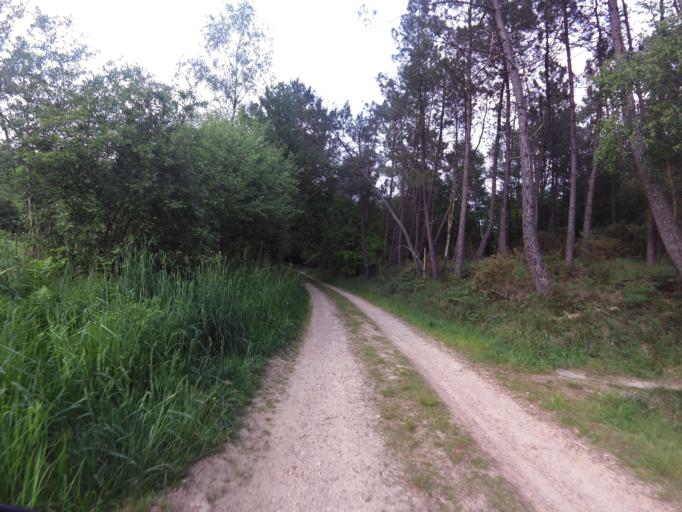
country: FR
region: Brittany
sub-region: Departement du Morbihan
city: Pleucadeuc
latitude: 47.7614
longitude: -2.4054
